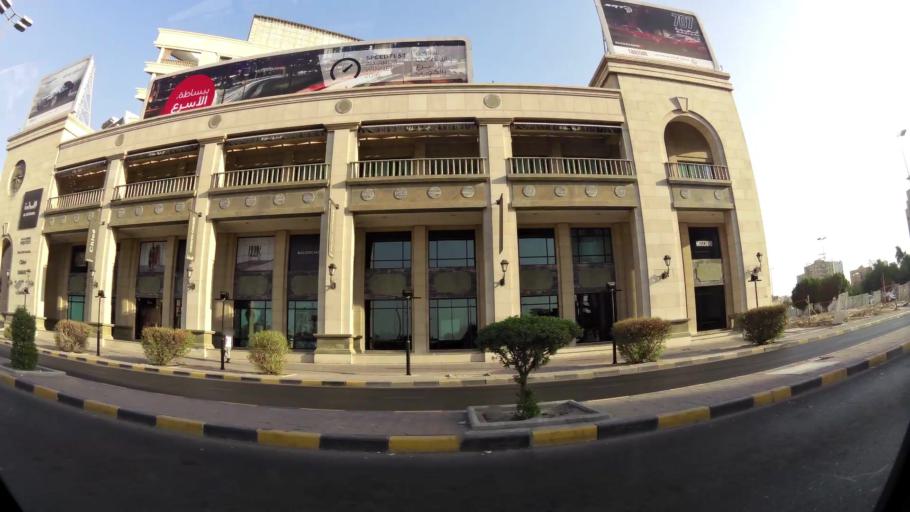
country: KW
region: Muhafazat Hawalli
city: As Salimiyah
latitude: 29.3402
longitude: 48.0702
